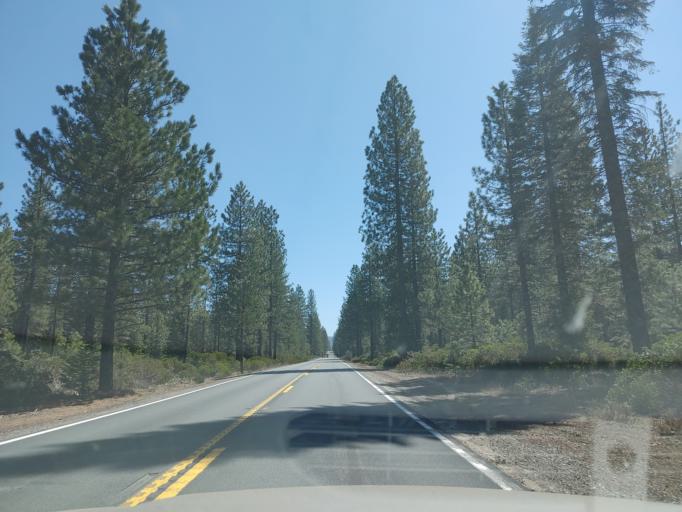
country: US
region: California
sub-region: Siskiyou County
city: McCloud
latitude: 41.2652
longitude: -121.8540
